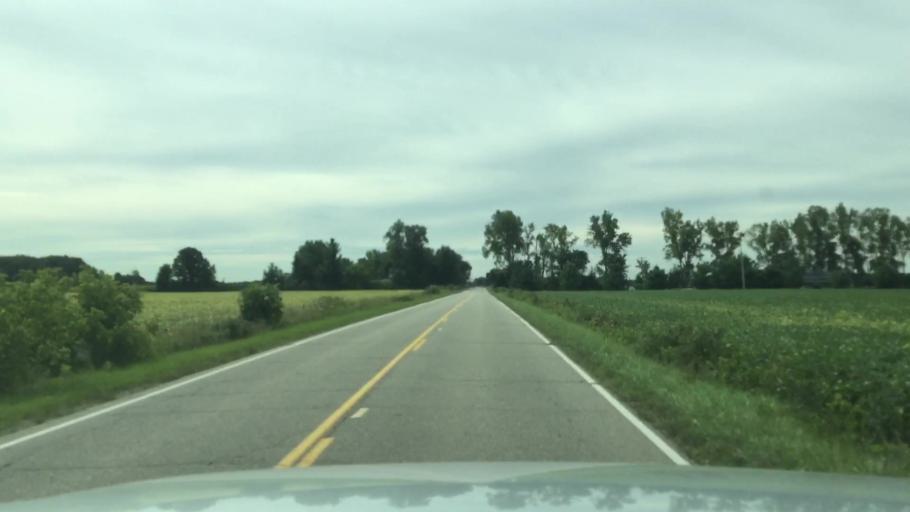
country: US
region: Michigan
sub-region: Genesee County
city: Montrose
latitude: 43.1012
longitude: -83.9877
